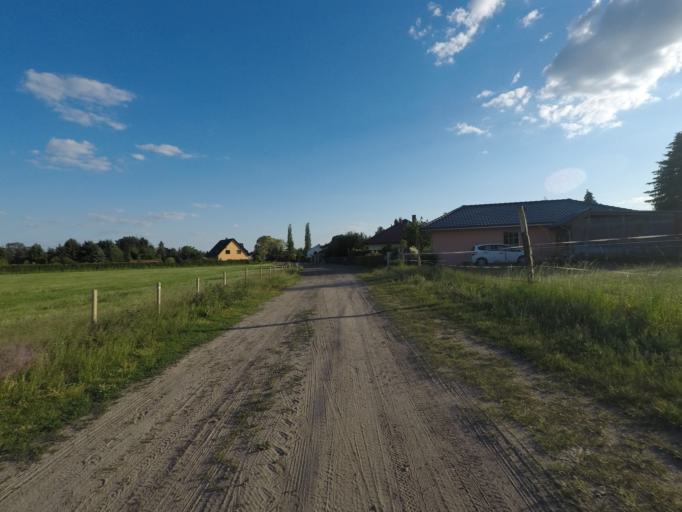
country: DE
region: Brandenburg
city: Melchow
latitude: 52.8572
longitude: 13.6839
